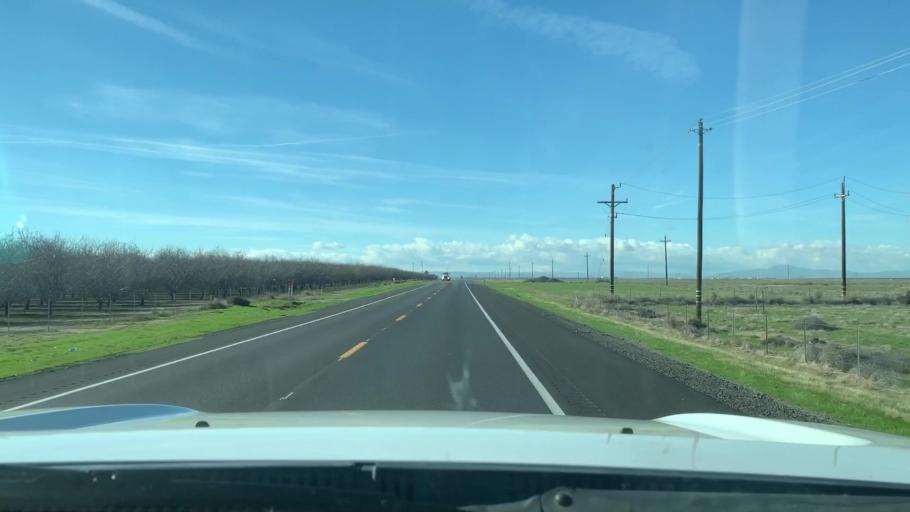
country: US
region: California
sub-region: Kern County
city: Lost Hills
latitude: 35.6157
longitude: -119.7513
